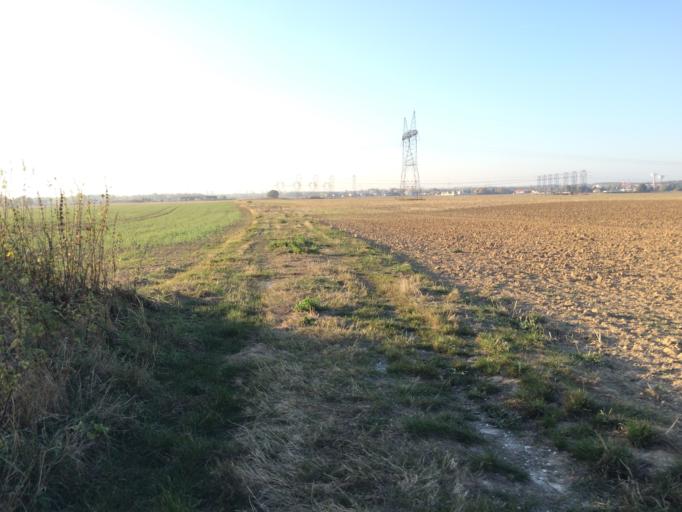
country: FR
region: Ile-de-France
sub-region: Departement de l'Essonne
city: Nozay
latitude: 48.6624
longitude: 2.2268
